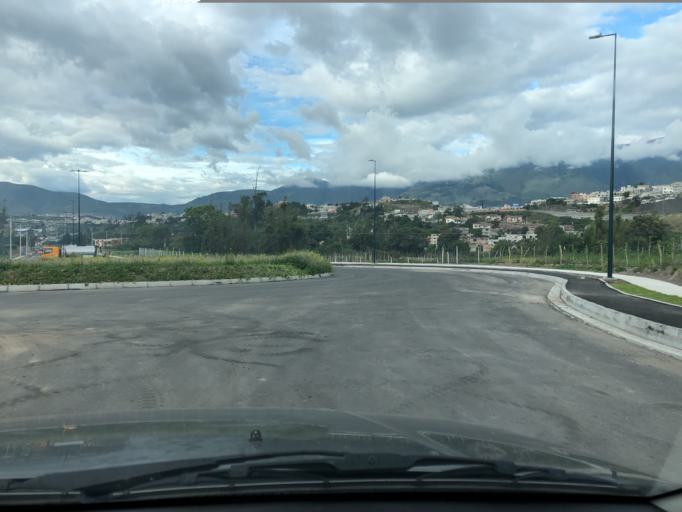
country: EC
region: Imbabura
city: Ibarra
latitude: 0.3398
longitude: -78.1553
